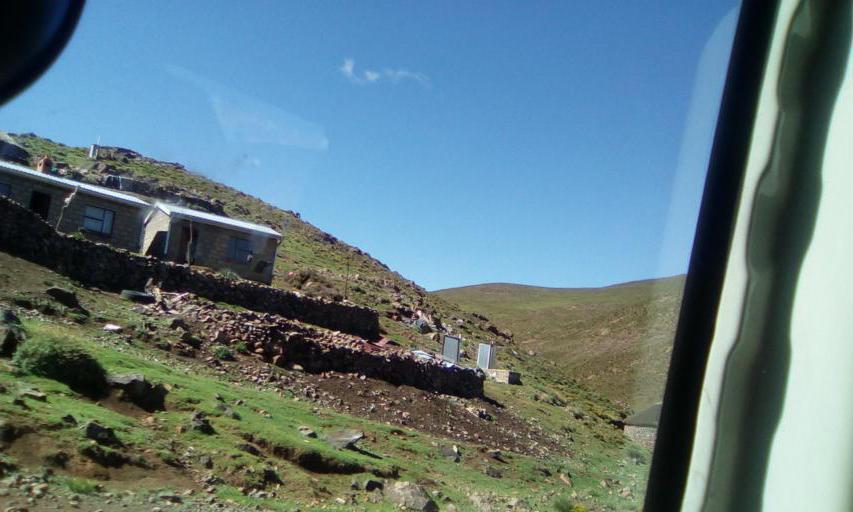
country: LS
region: Maseru
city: Nako
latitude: -29.8912
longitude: 28.1183
